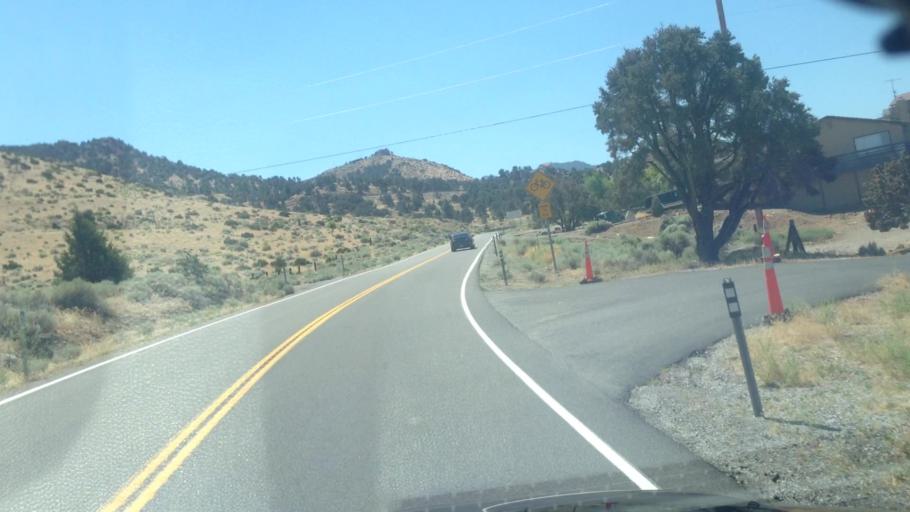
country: US
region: Nevada
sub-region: Storey County
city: Virginia City
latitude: 39.3897
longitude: -119.7155
